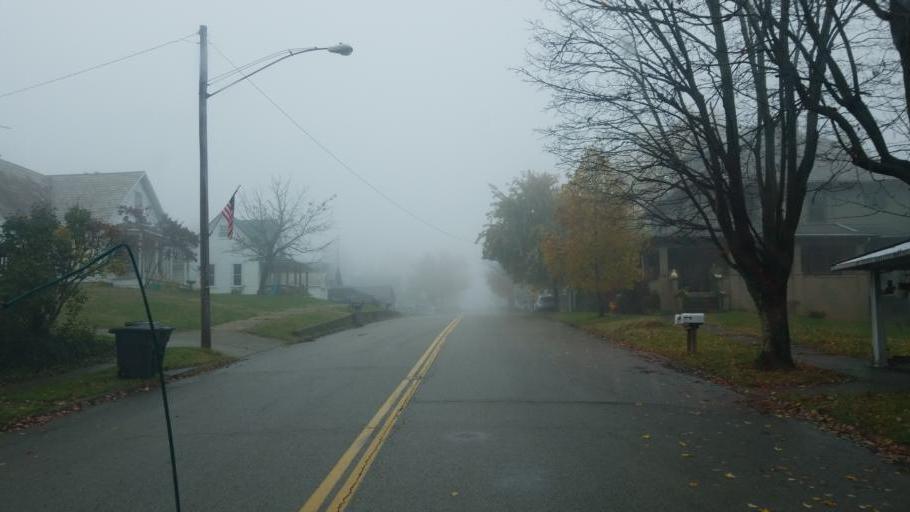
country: US
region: Ohio
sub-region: Morgan County
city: McConnelsville
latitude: 39.5755
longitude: -81.8564
